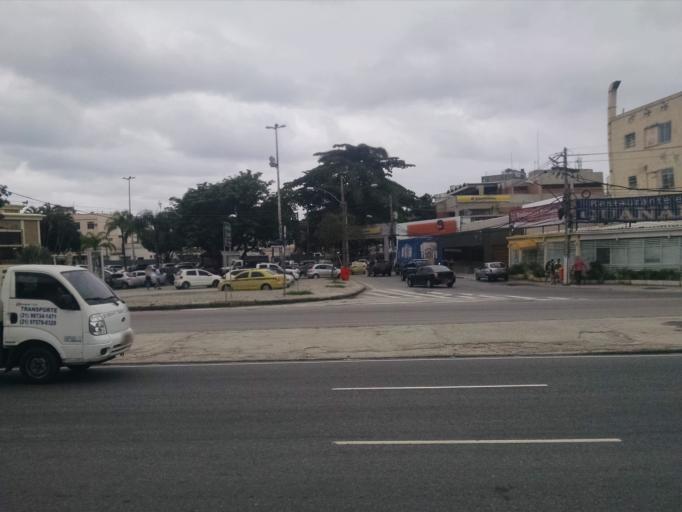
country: BR
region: Rio de Janeiro
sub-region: Rio De Janeiro
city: Rio de Janeiro
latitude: -23.0073
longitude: -43.3046
